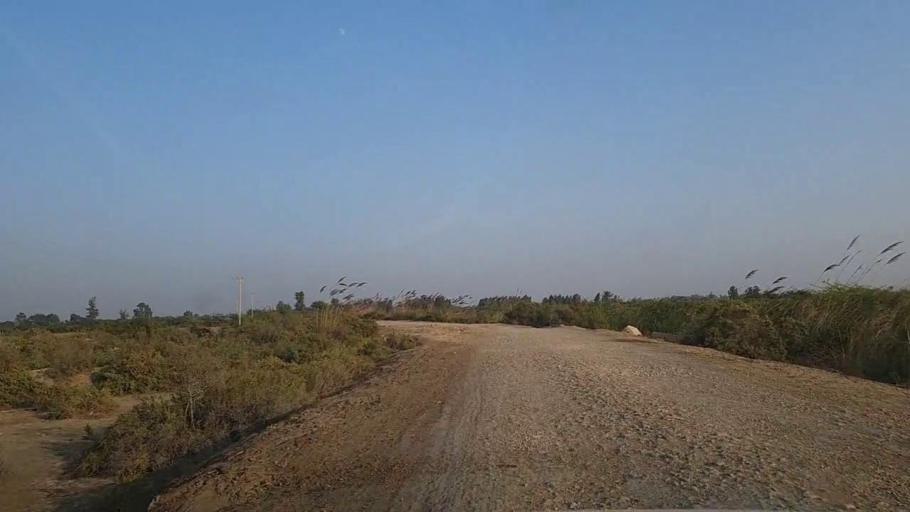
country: PK
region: Sindh
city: Keti Bandar
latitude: 24.2770
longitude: 67.6484
